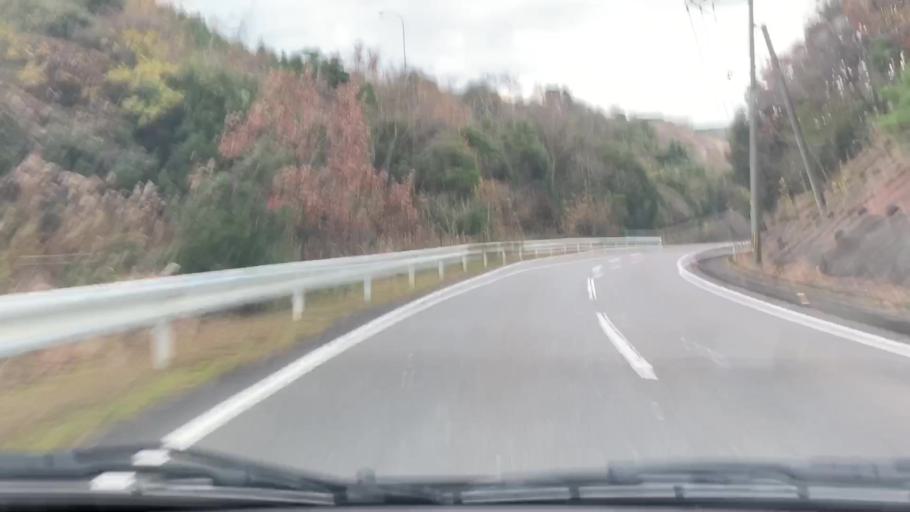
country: JP
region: Saga Prefecture
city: Ureshinomachi-shimojuku
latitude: 33.1130
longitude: 129.9761
